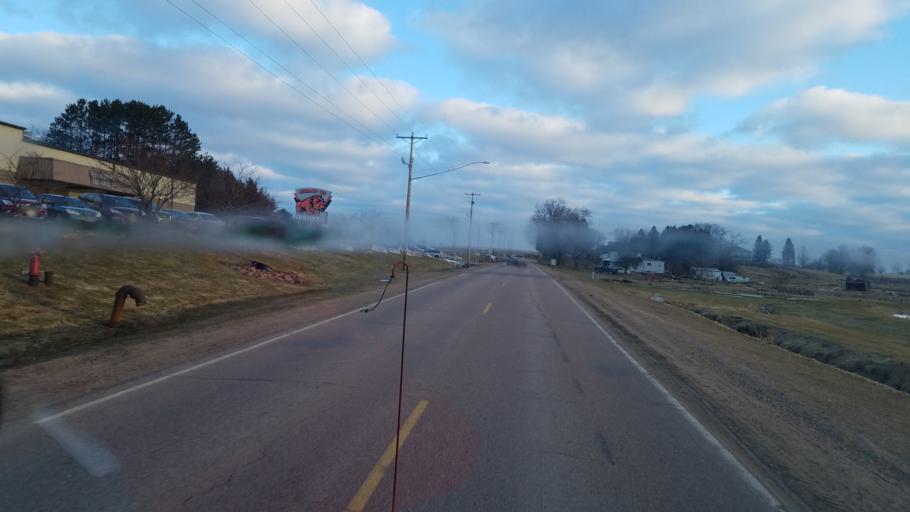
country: US
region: Wisconsin
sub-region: Clark County
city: Neillsville
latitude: 44.5924
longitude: -90.4615
